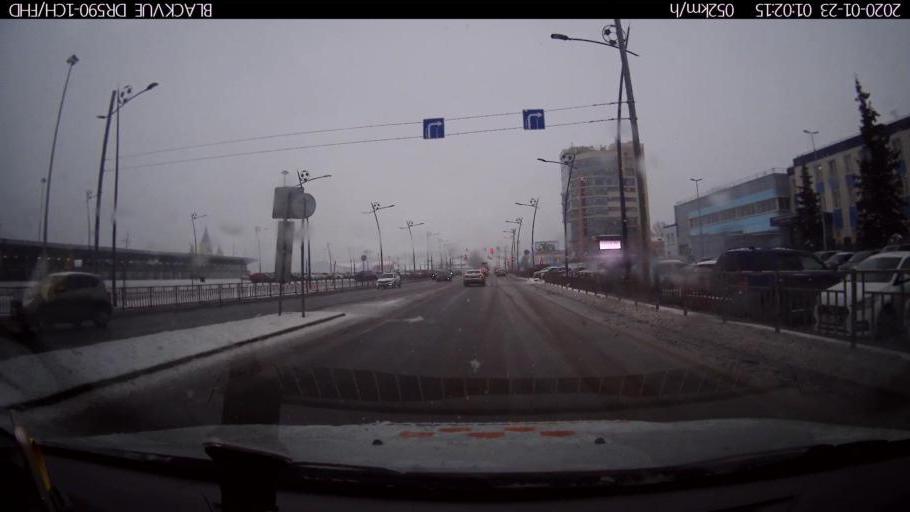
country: RU
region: Nizjnij Novgorod
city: Nizhniy Novgorod
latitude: 56.3347
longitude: 43.9633
